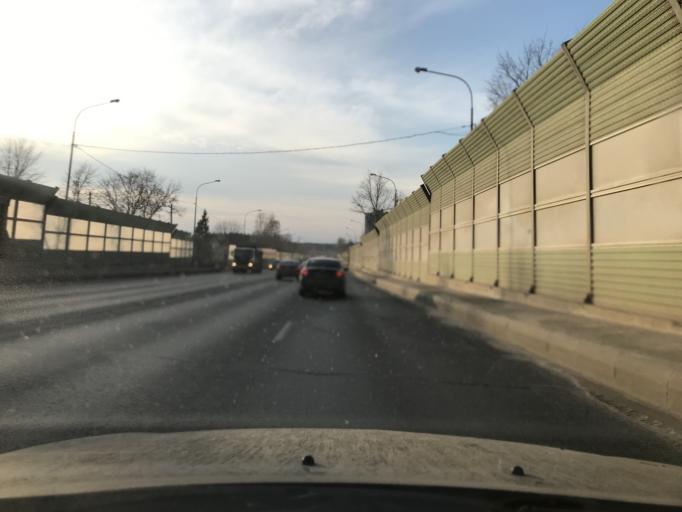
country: RU
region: Kaluga
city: Mstikhino
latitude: 54.5333
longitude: 36.1665
